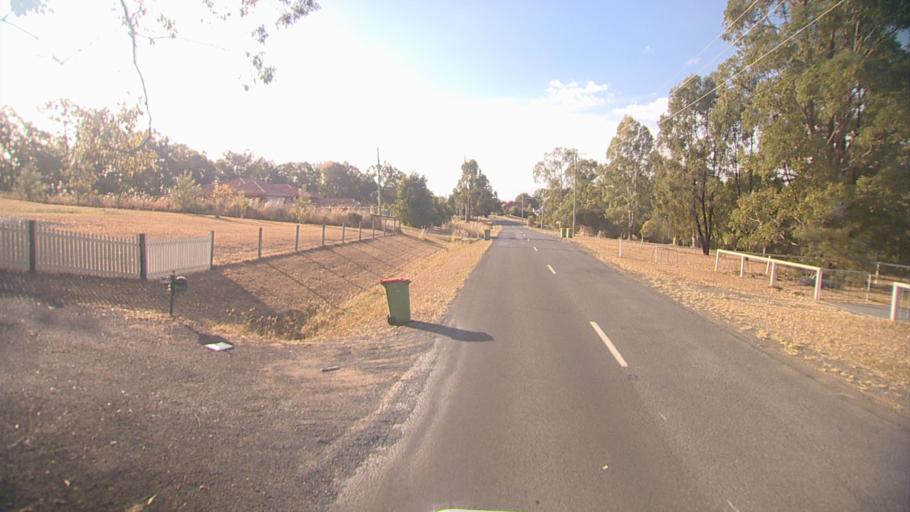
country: AU
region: Queensland
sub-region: Logan
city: Cedar Vale
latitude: -27.8758
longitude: 153.0107
